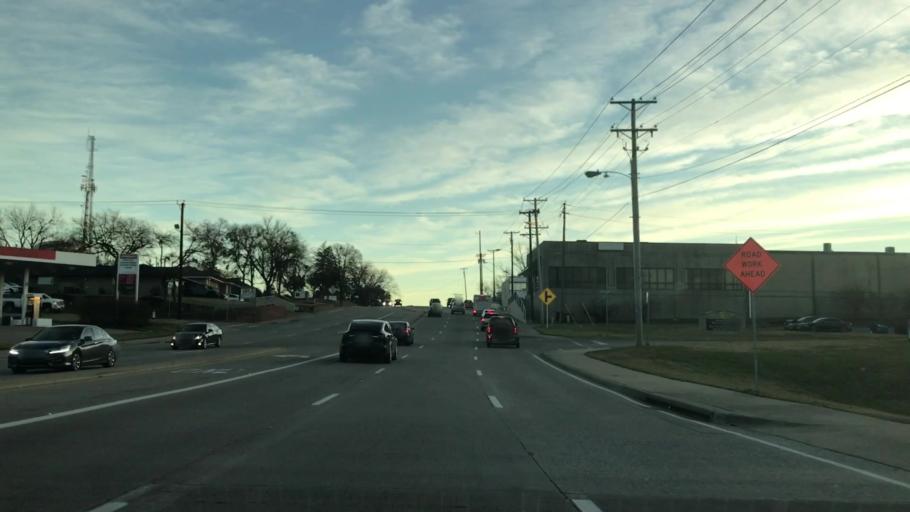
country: US
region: Texas
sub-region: Rockwall County
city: Rockwall
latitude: 32.9278
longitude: -96.4604
